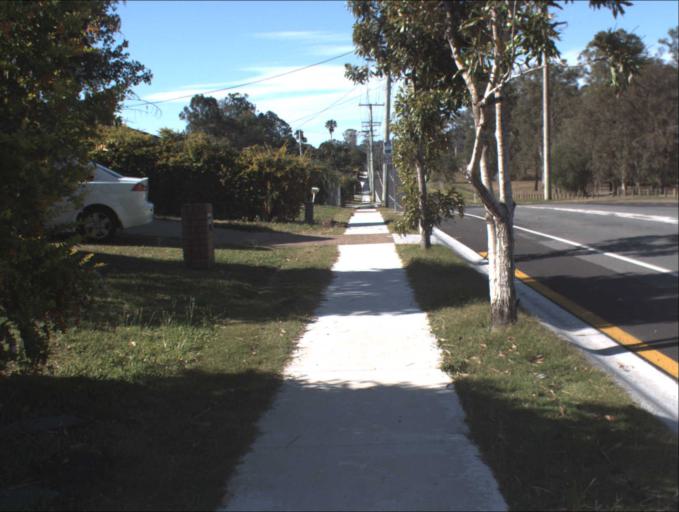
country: AU
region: Queensland
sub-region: Logan
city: Slacks Creek
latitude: -27.6523
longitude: 153.1351
